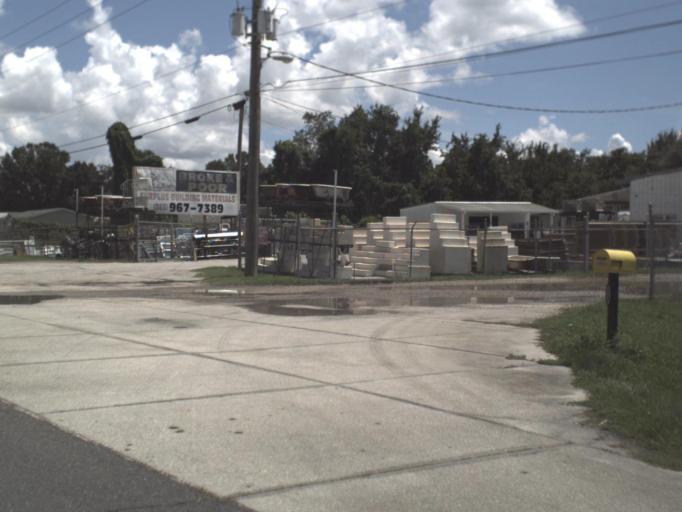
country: US
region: Florida
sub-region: Polk County
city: Auburndale
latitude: 28.0562
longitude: -81.8239
